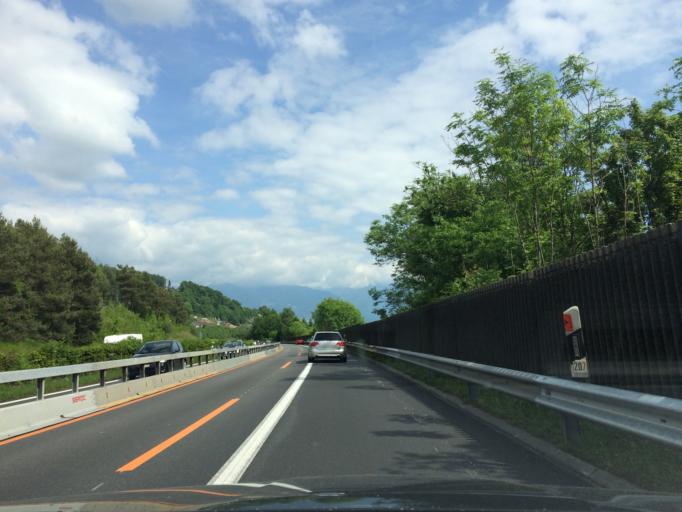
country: CH
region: Vaud
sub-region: Lavaux-Oron District
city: Chexbres
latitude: 46.4832
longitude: 6.7812
